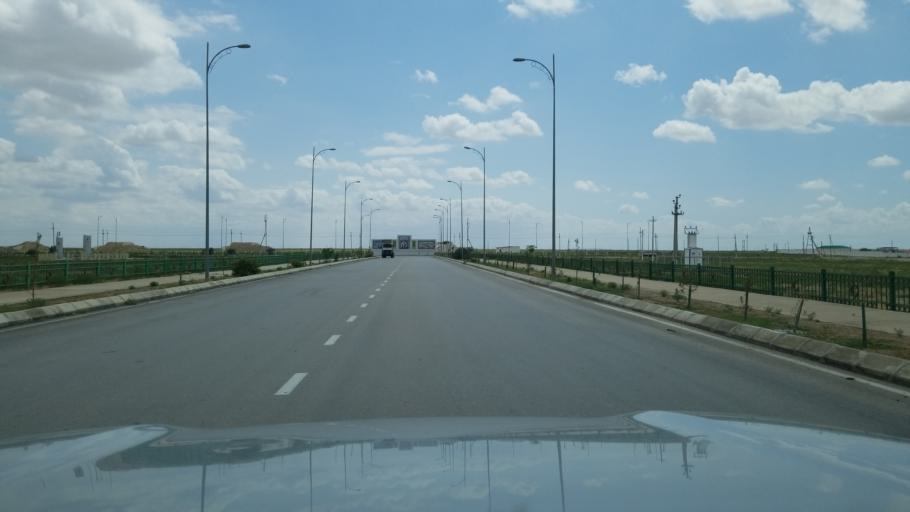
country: TM
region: Balkan
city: Balkanabat
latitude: 39.4882
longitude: 54.3755
